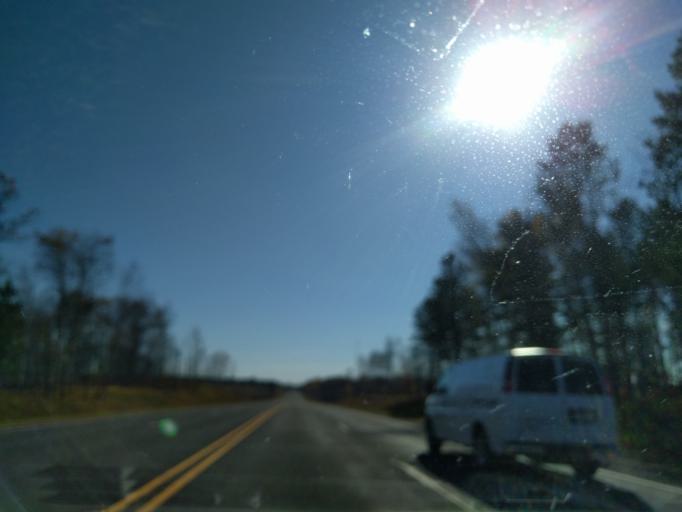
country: US
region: Michigan
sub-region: Iron County
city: Crystal Falls
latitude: 46.2333
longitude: -88.0078
